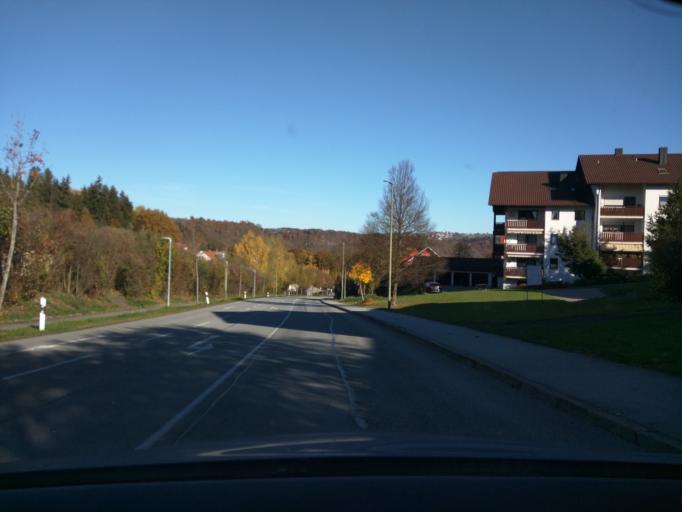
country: DE
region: Bavaria
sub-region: Lower Bavaria
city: Salzweg
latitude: 48.5853
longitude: 13.4927
